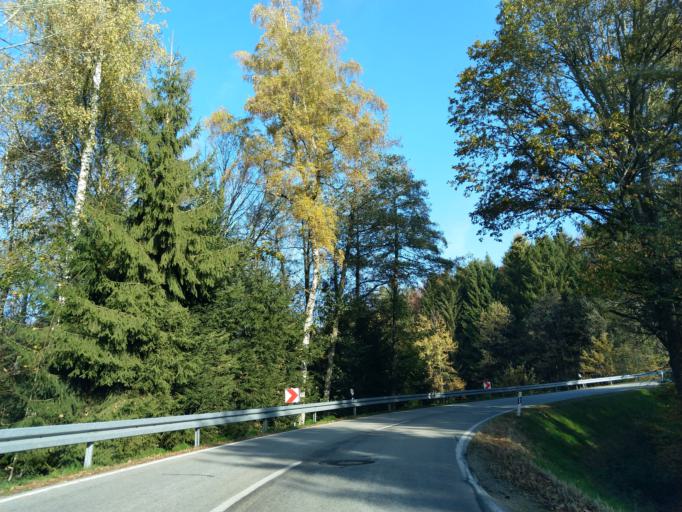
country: DE
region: Bavaria
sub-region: Lower Bavaria
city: Lalling
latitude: 48.8570
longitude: 13.1392
